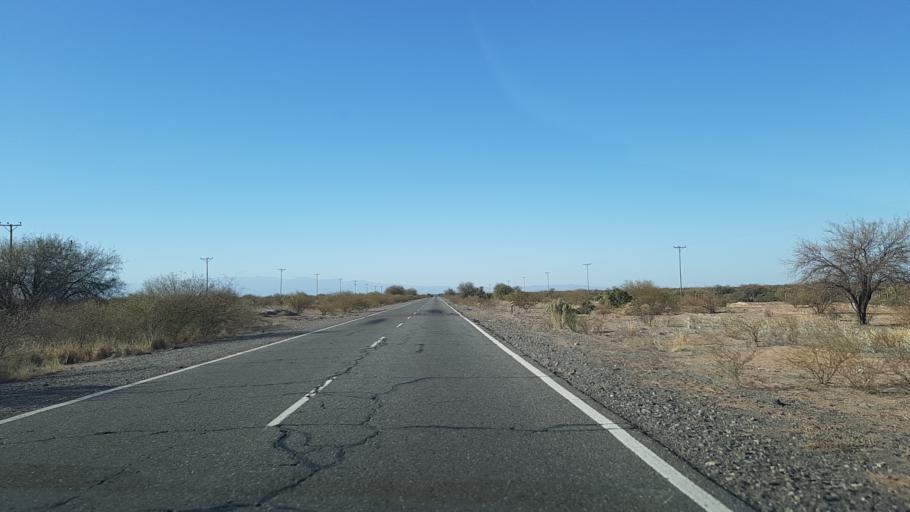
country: AR
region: San Juan
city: Caucete
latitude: -31.6384
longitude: -67.7518
